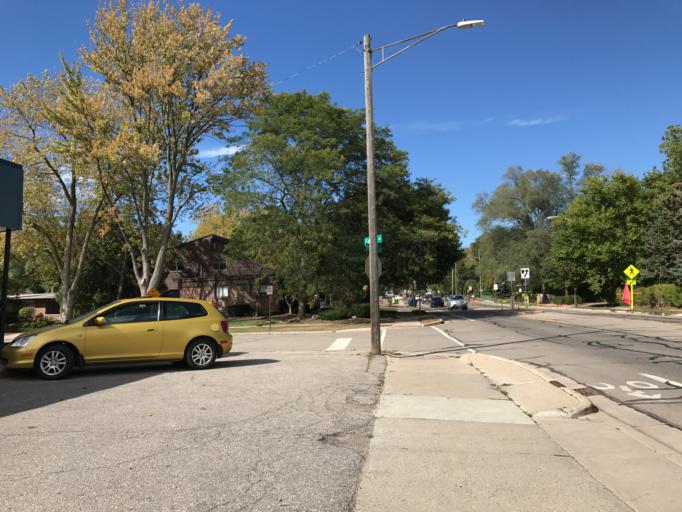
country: US
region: Michigan
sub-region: Washtenaw County
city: Ann Arbor
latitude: 42.2579
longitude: -83.7280
